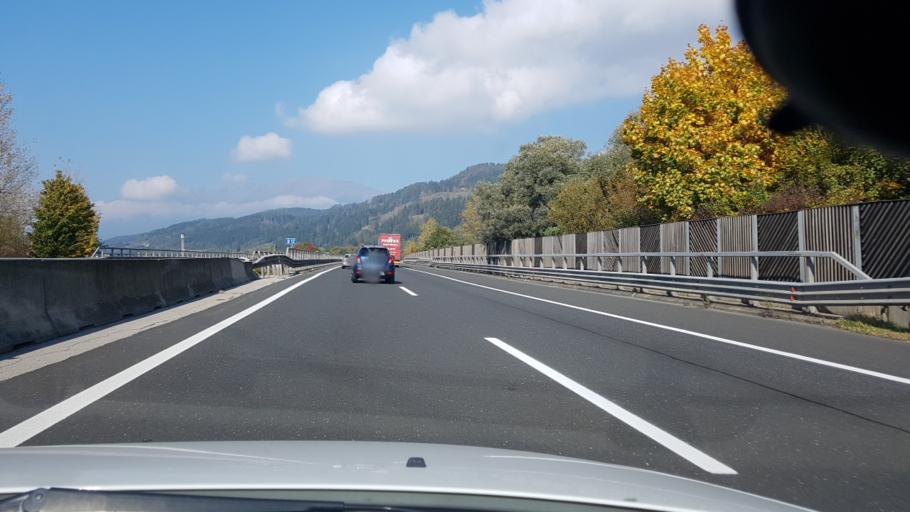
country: AT
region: Carinthia
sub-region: Politischer Bezirk Spittal an der Drau
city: Millstatt
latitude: 46.7705
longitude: 13.5533
